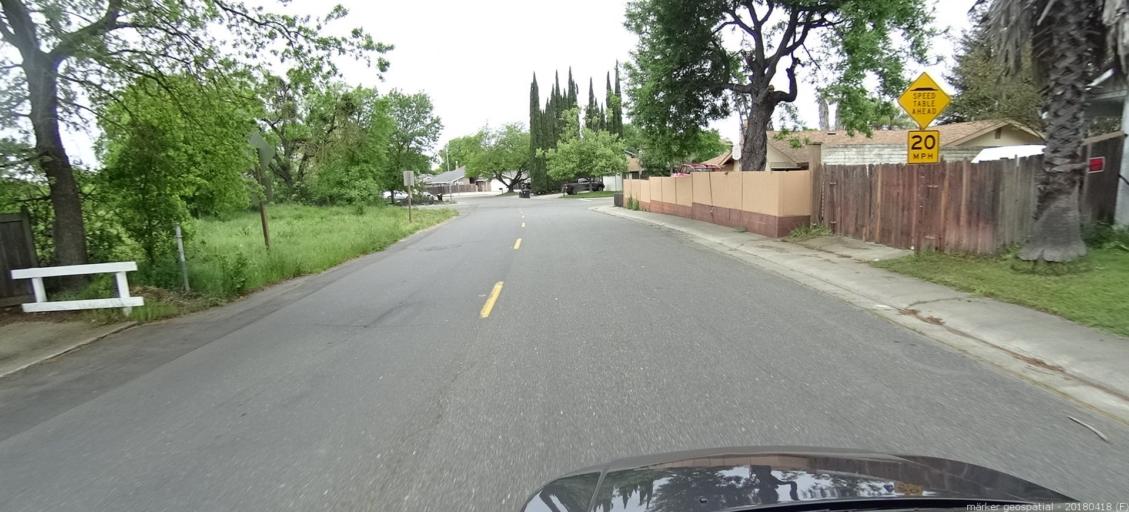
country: US
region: California
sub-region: Sacramento County
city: La Riviera
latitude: 38.5703
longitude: -121.3456
